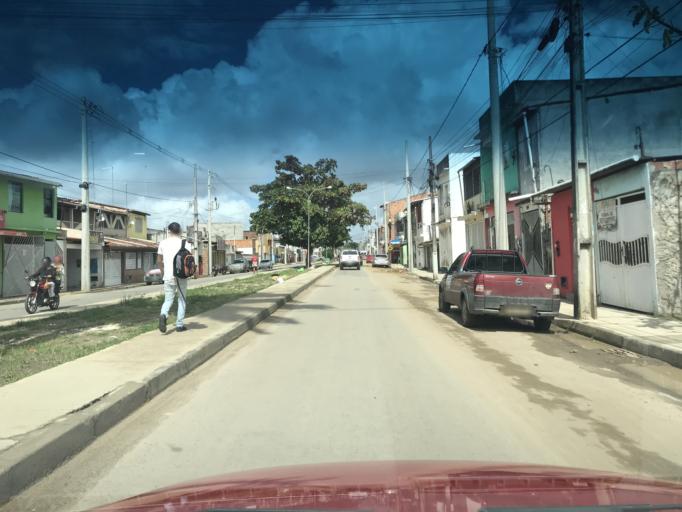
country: BR
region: Bahia
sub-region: Santo Antonio De Jesus
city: Santo Antonio de Jesus
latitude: -12.9751
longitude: -39.2742
